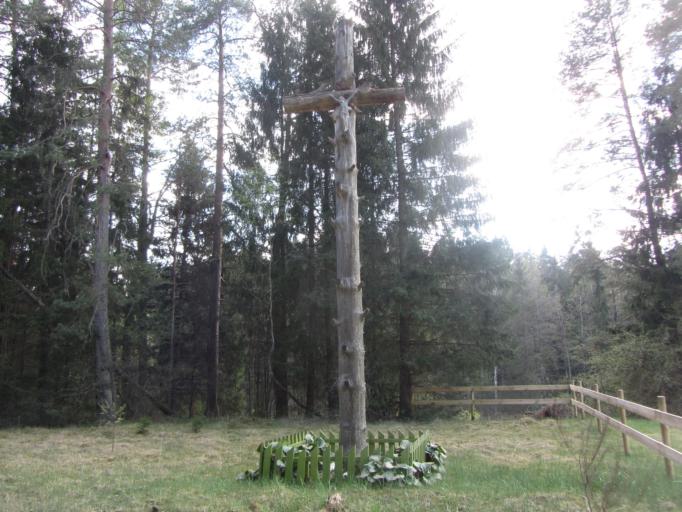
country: LT
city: Svencioneliai
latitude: 55.1664
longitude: 25.8402
